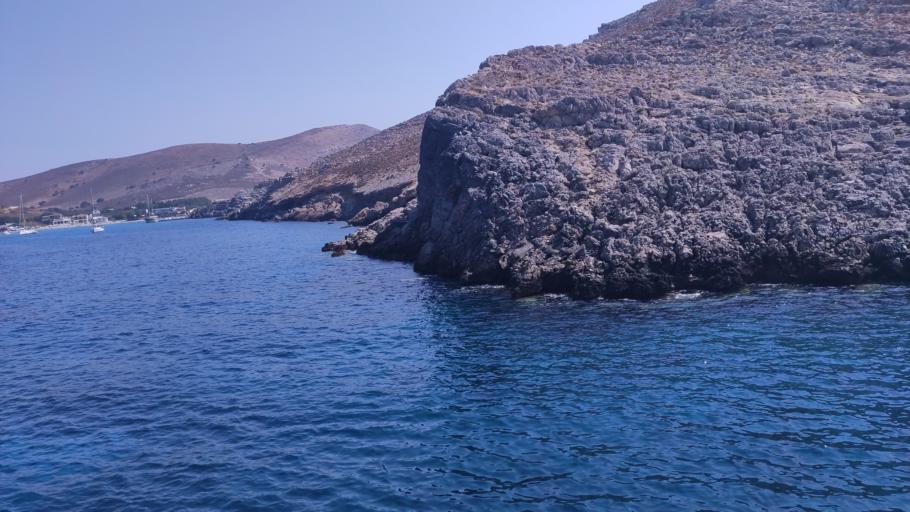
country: GR
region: South Aegean
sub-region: Nomos Dodekanisou
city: Pylion
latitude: 36.9277
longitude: 27.1302
